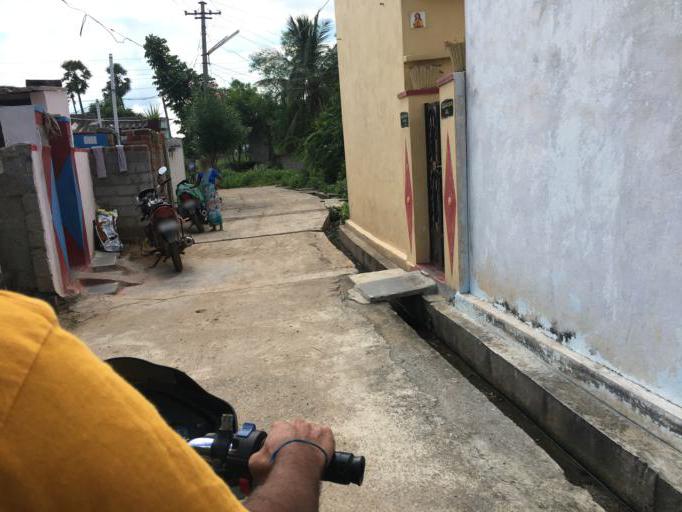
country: IN
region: Telangana
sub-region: Nalgonda
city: Nalgonda
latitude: 17.1683
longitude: 79.4205
